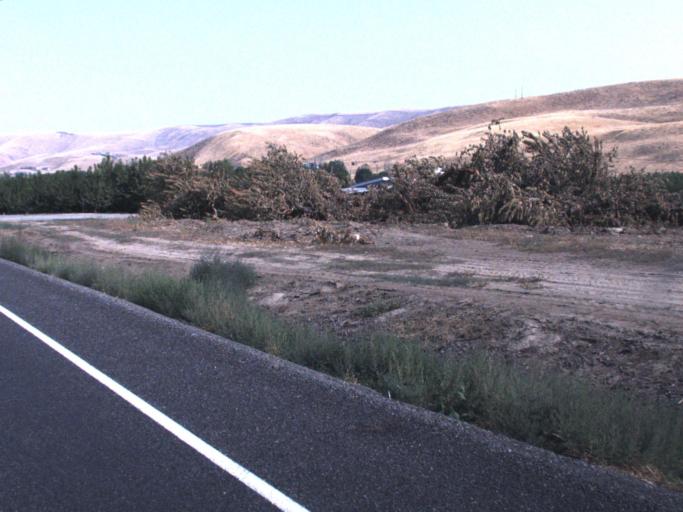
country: US
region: Washington
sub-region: Yakima County
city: Grandview
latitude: 46.1858
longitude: -119.8579
